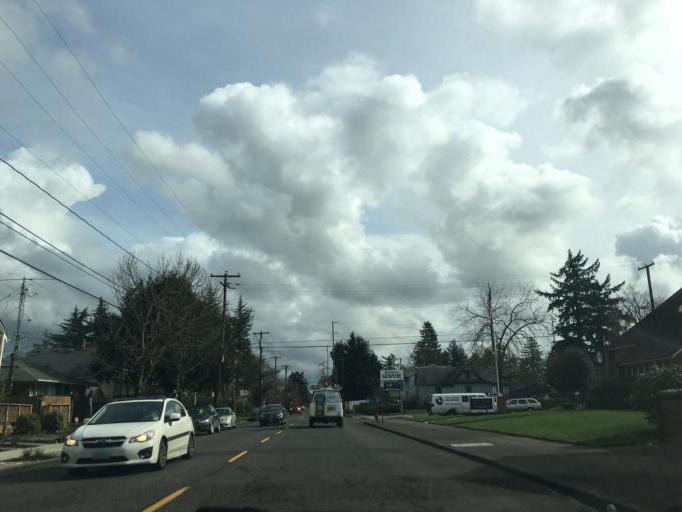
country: US
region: Oregon
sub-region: Multnomah County
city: Lents
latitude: 45.4903
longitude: -122.5934
